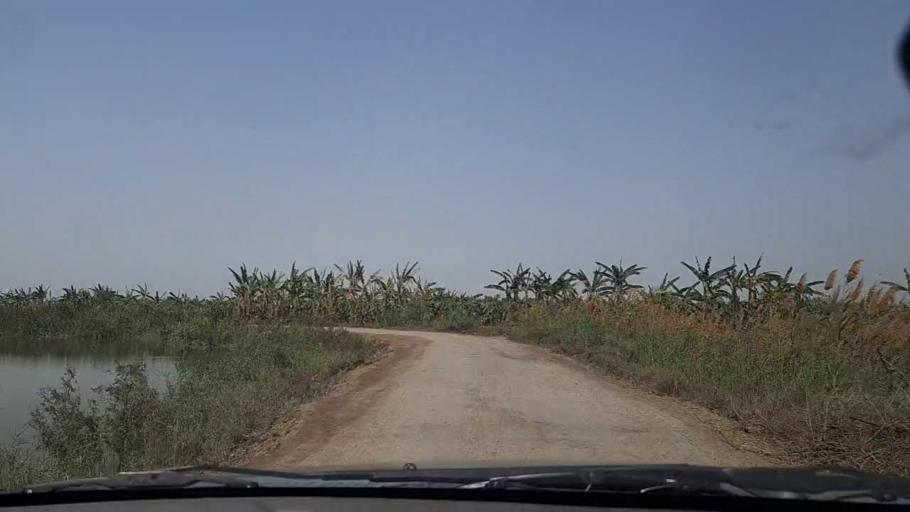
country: PK
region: Sindh
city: Keti Bandar
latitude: 24.2784
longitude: 67.6714
